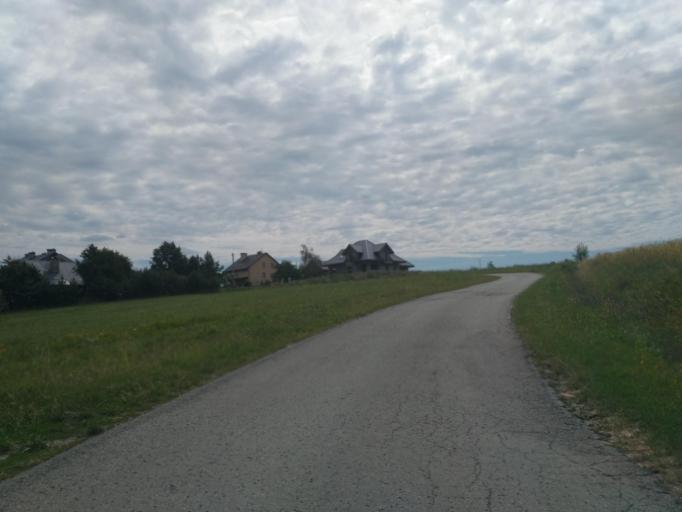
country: PL
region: Subcarpathian Voivodeship
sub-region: Powiat rzeszowski
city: Straszydle
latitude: 49.8828
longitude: 21.9837
